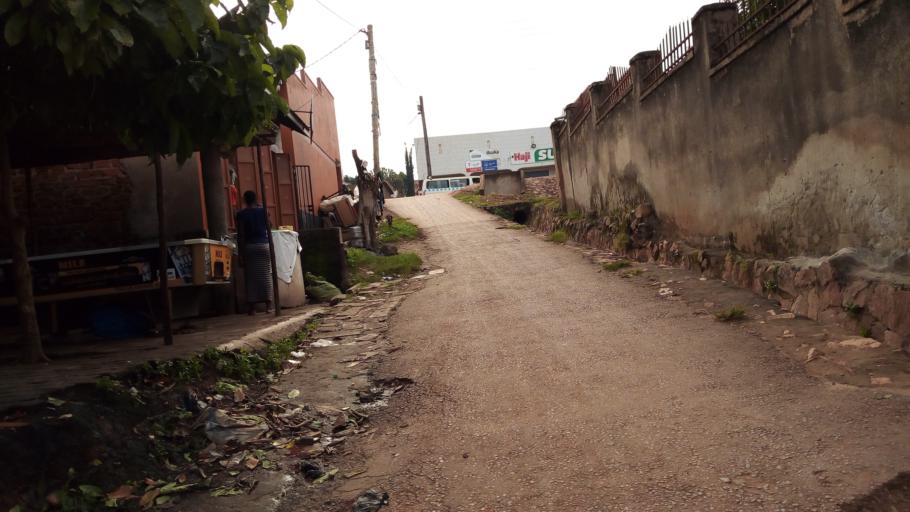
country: UG
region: Central Region
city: Kampala Central Division
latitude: 0.3695
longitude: 32.5540
